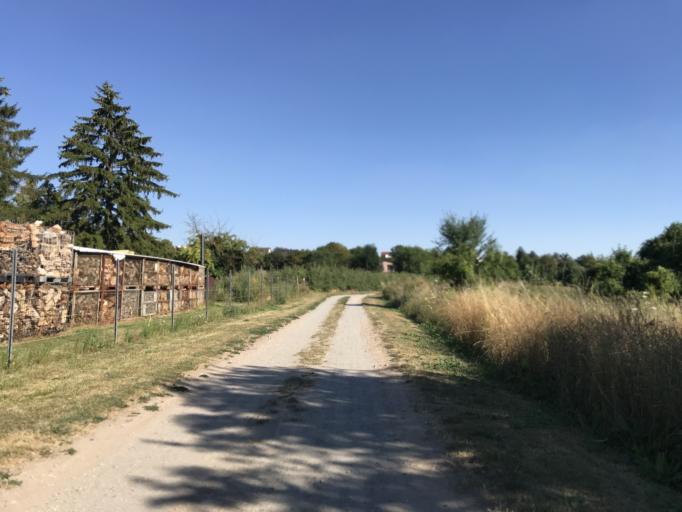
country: DE
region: Rheinland-Pfalz
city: Schwabenheim
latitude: 49.9330
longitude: 8.0894
